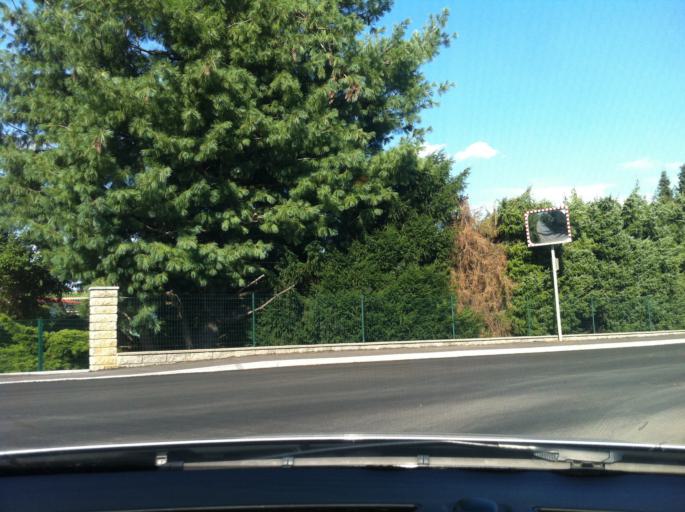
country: AT
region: Styria
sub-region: Politischer Bezirk Weiz
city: Krottendorf
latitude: 47.2022
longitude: 15.6426
